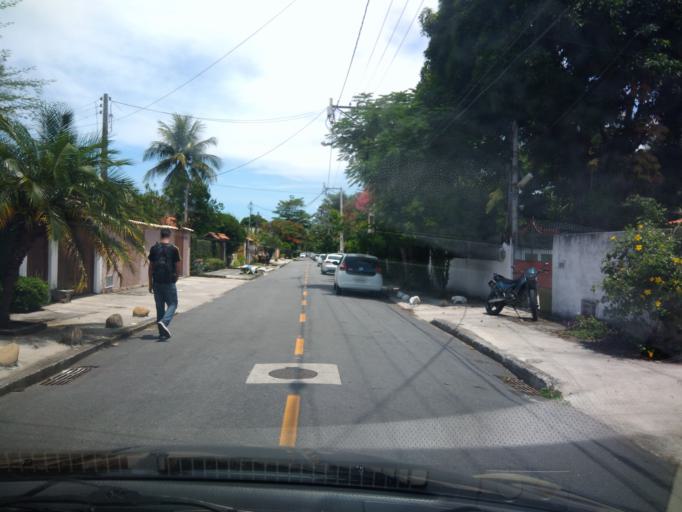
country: BR
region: Rio de Janeiro
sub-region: Niteroi
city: Niteroi
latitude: -22.9307
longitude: -43.0707
